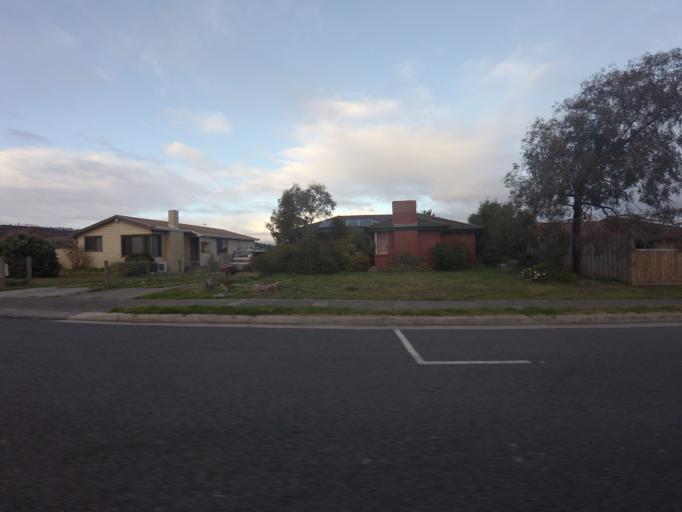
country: AU
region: Tasmania
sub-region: Clarence
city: Rokeby
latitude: -42.9024
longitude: 147.4351
